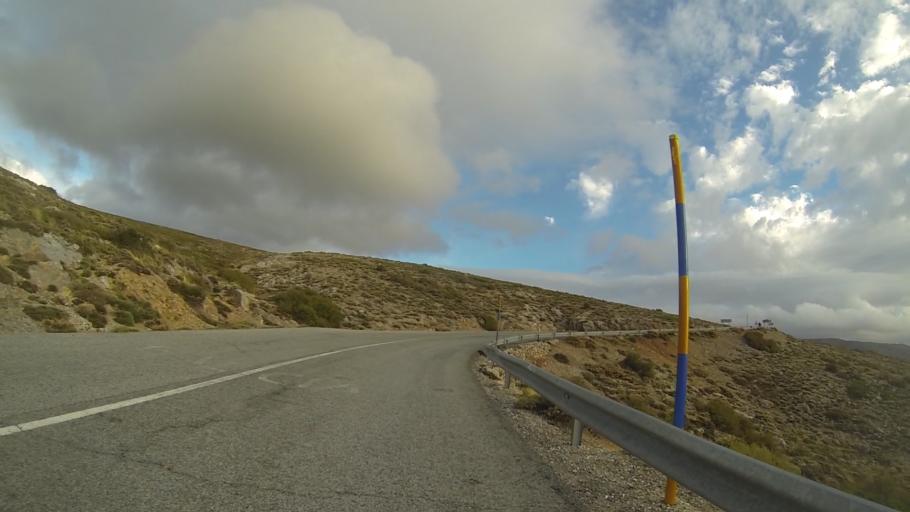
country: ES
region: Andalusia
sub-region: Provincia de Granada
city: Guejar-Sierra
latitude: 37.1197
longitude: -3.4311
